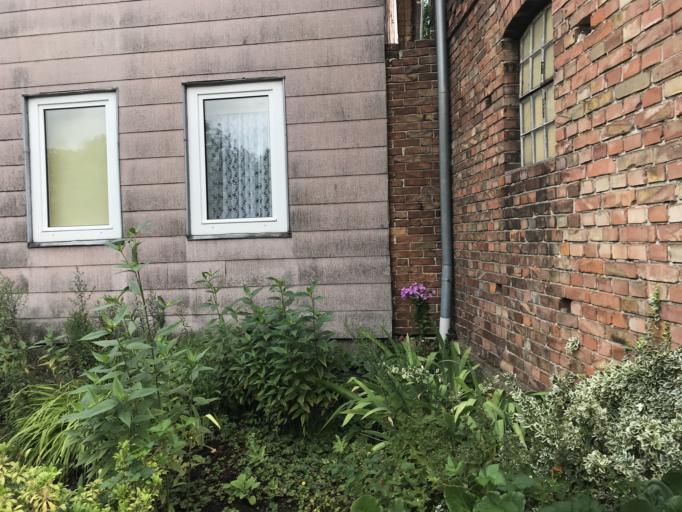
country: DE
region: Lower Saxony
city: Suderburg
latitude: 52.8964
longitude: 10.4511
